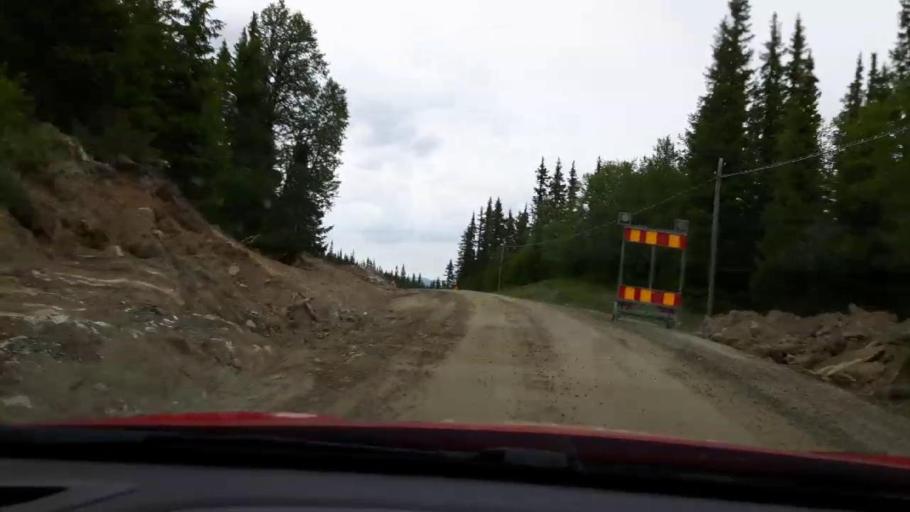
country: SE
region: Jaemtland
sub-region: Are Kommun
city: Are
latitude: 62.8236
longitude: 12.8135
